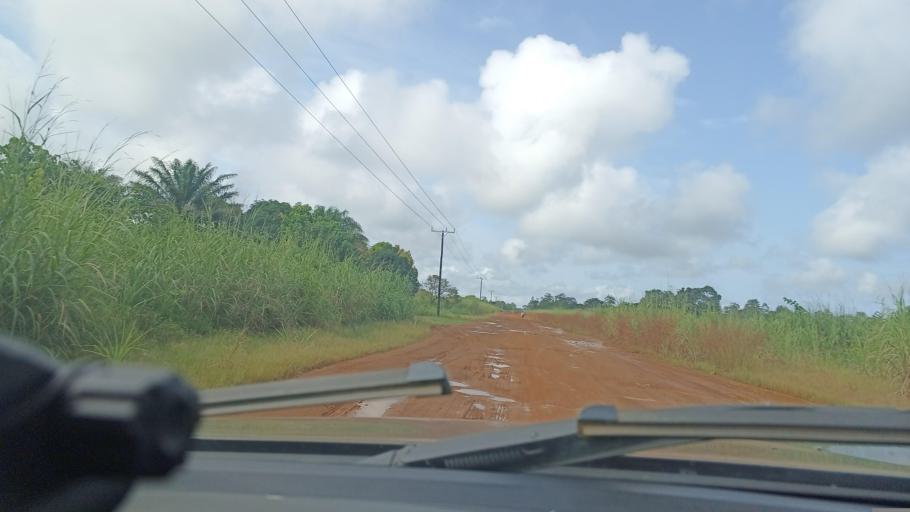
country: LR
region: Grand Cape Mount
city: Robertsport
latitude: 6.6933
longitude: -11.1076
